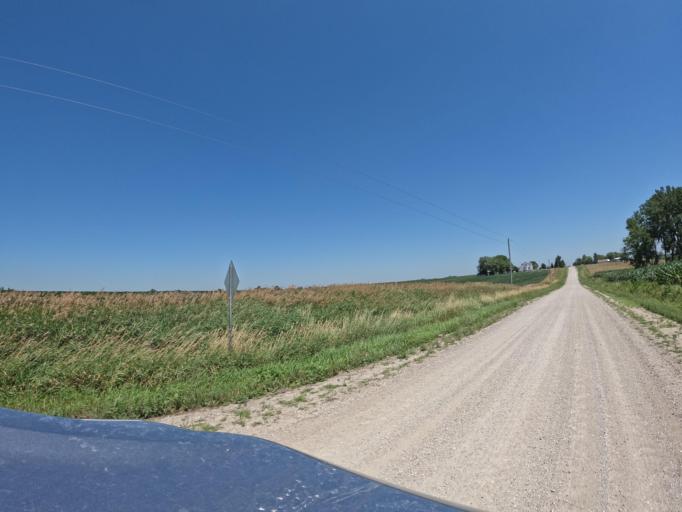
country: US
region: Iowa
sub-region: Keokuk County
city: Sigourney
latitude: 41.4234
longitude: -92.3518
